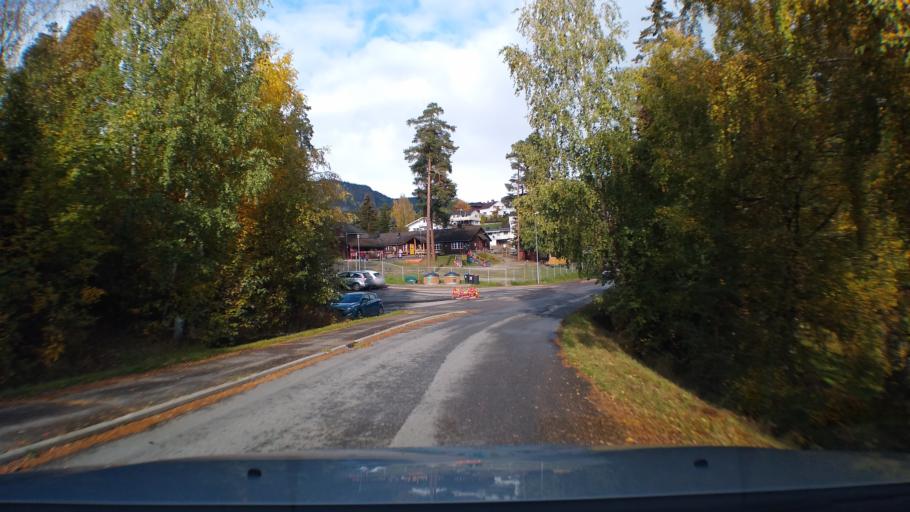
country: NO
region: Oppland
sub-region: Ringebu
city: Ringebu
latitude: 61.5329
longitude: 10.1356
